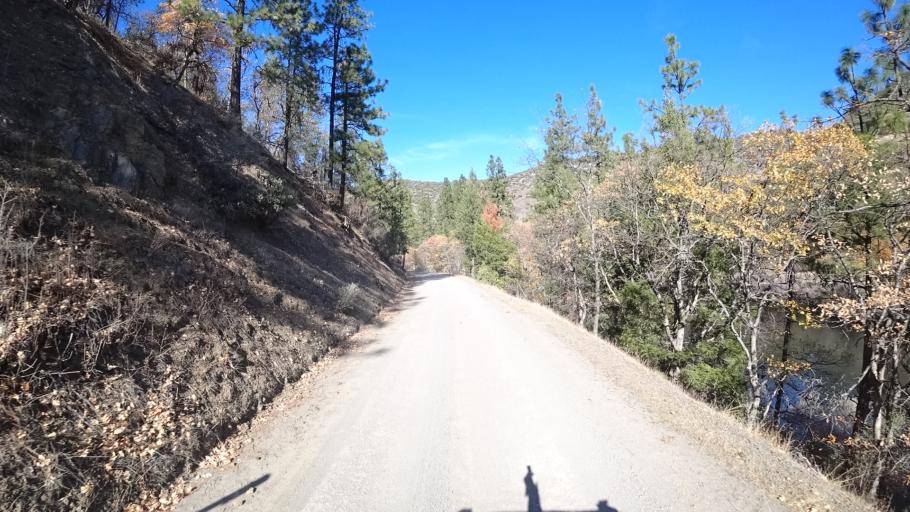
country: US
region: California
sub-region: Siskiyou County
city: Yreka
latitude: 41.8526
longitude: -122.6954
